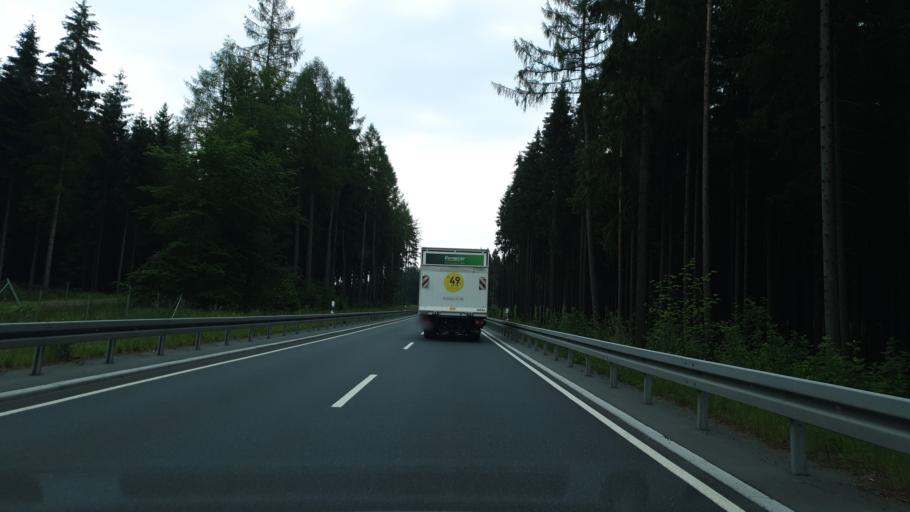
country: DE
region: Saxony
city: Tannenbergsthal
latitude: 50.4650
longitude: 12.4385
